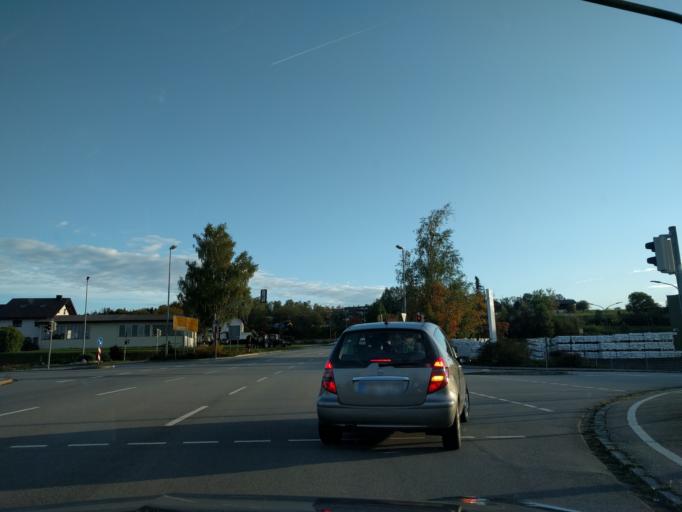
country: DE
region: Bavaria
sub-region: Lower Bavaria
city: Viechtach
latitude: 49.0796
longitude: 12.8762
